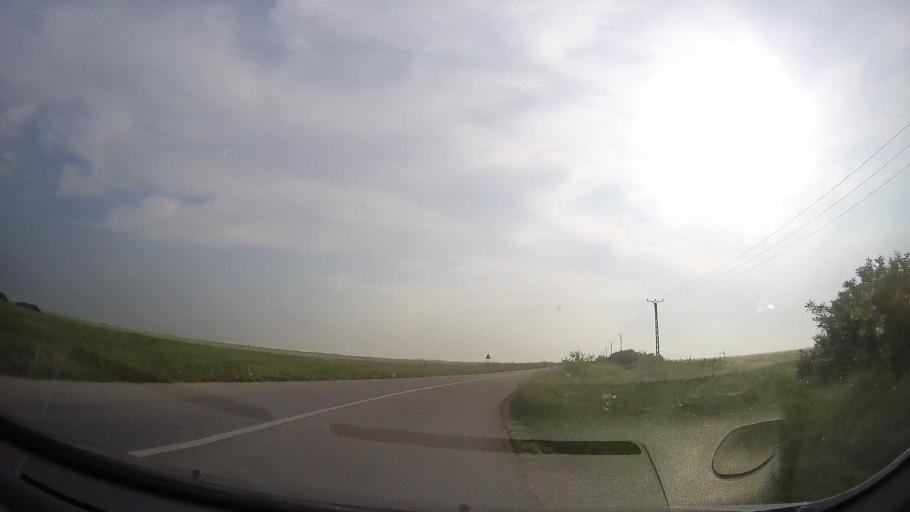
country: RO
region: Timis
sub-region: Comuna Foeni
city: Foeni
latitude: 45.5165
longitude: 20.8966
